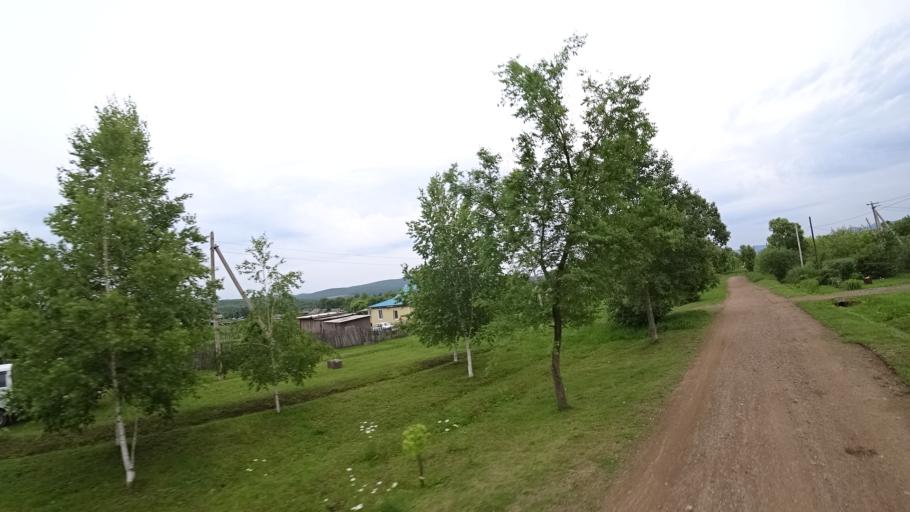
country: RU
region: Primorskiy
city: Novosysoyevka
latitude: 44.2315
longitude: 133.3658
